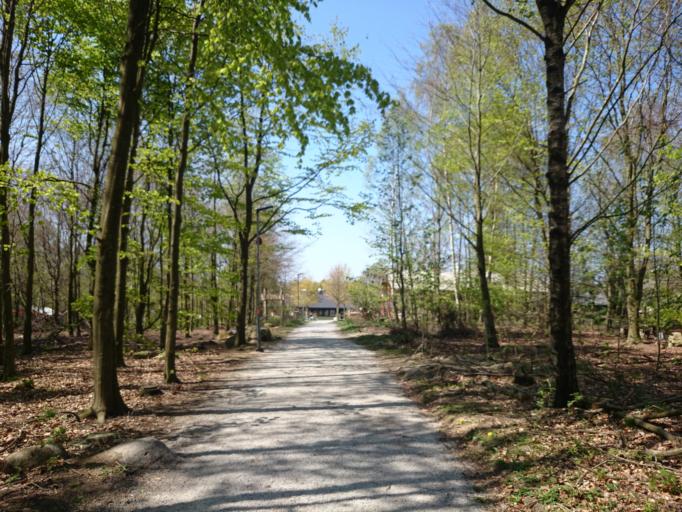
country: SE
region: Skane
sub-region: Lunds Kommun
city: Genarp
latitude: 55.6921
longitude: 13.3617
